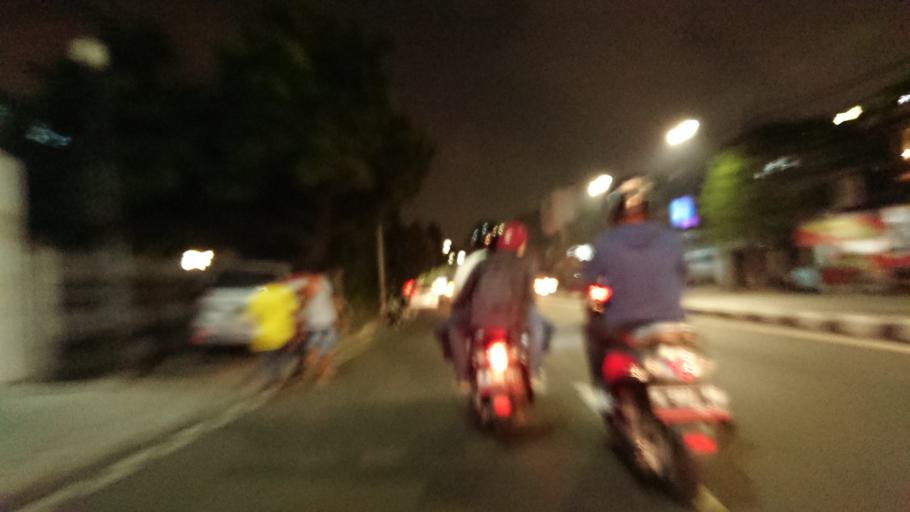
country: ID
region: Jakarta Raya
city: Jakarta
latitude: -6.1910
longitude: 106.8062
